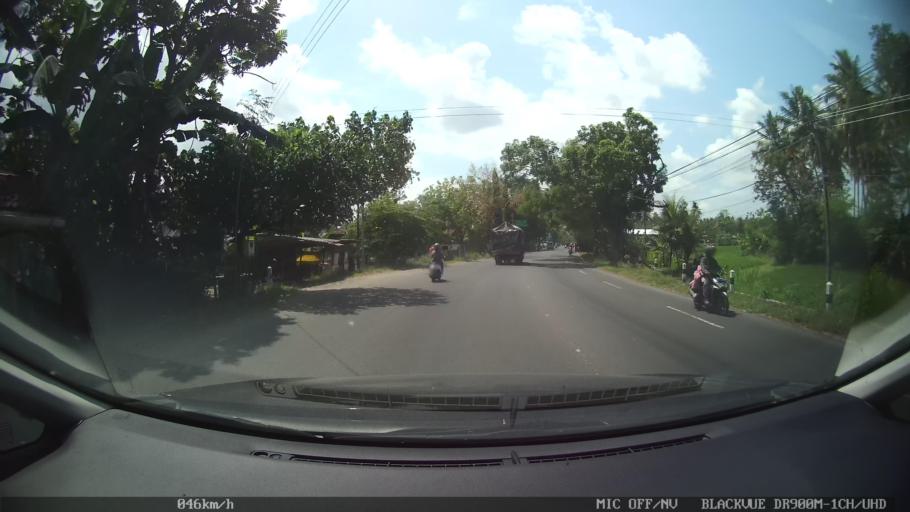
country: ID
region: Daerah Istimewa Yogyakarta
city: Pandak
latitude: -7.9132
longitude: 110.2873
